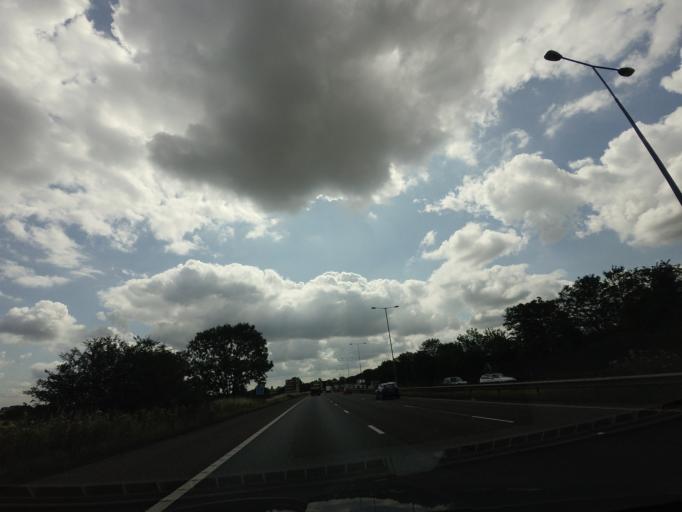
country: GB
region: England
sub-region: Borough of Wigan
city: Shevington
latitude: 53.5476
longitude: -2.6988
